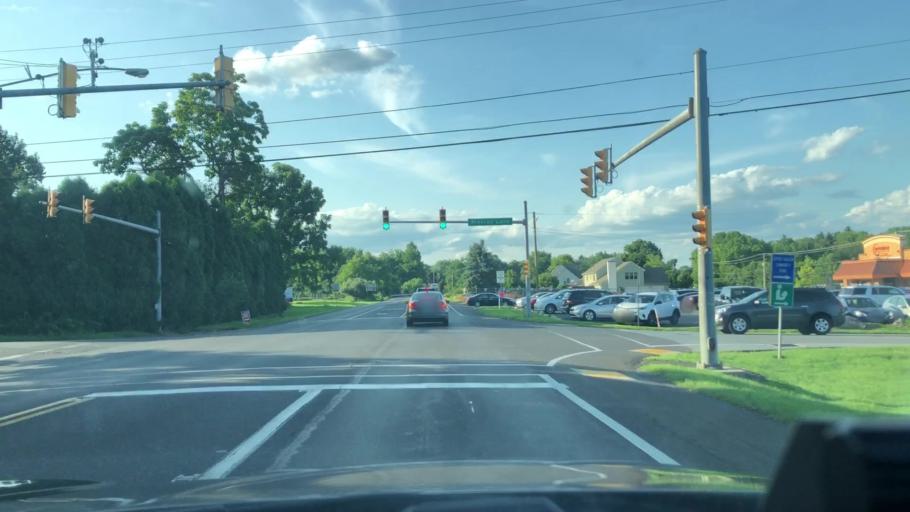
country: US
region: Pennsylvania
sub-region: Lehigh County
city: Coopersburg
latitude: 40.5357
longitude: -75.3956
